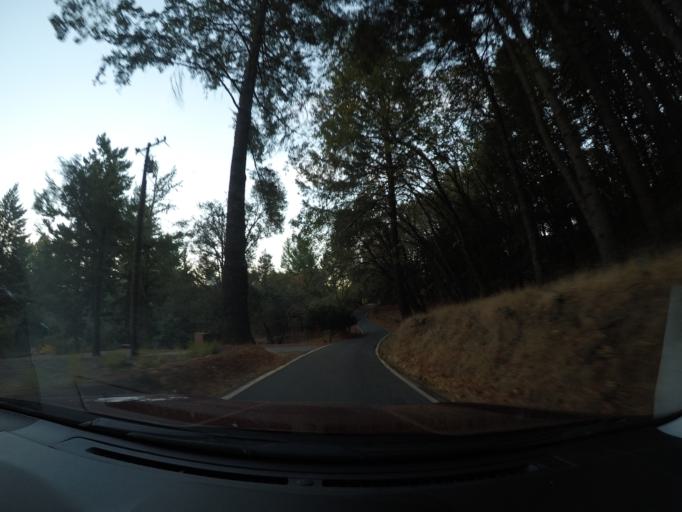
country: US
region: California
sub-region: Santa Clara County
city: Monte Sereno
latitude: 37.1943
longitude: -122.0384
